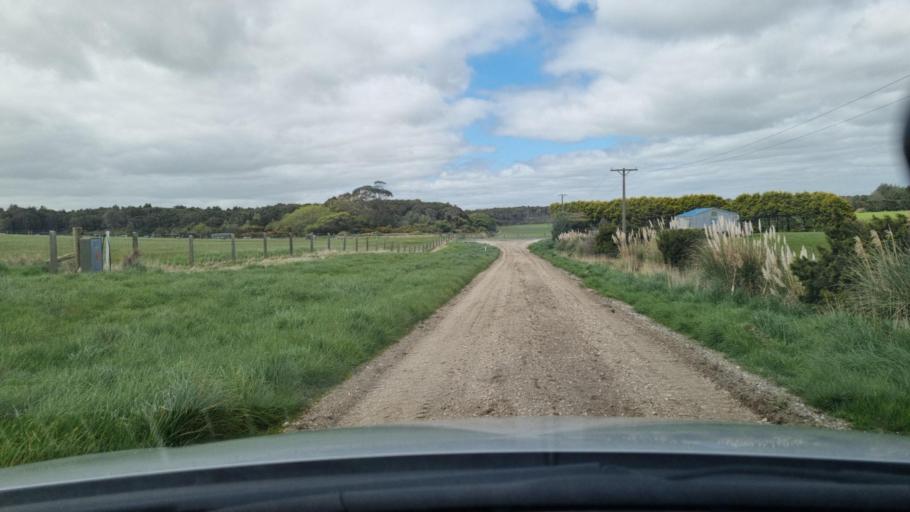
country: NZ
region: Southland
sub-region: Invercargill City
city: Invercargill
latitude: -46.4343
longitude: 168.4125
